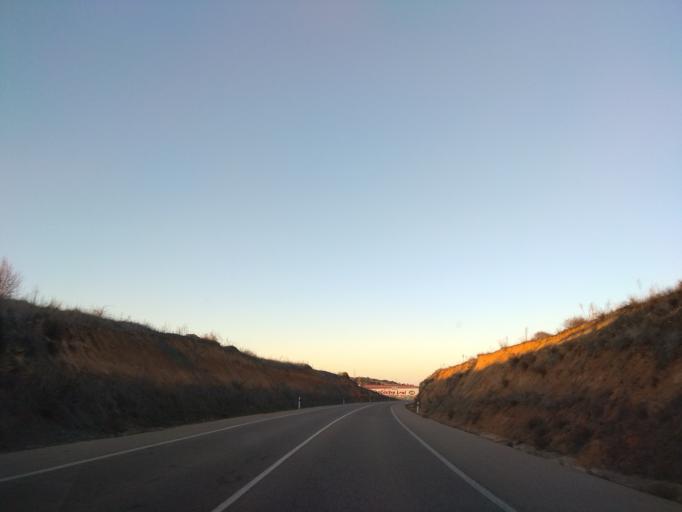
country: ES
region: Castille and Leon
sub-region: Provincia de Burgos
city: Aranda de Duero
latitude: 41.6856
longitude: -3.6878
